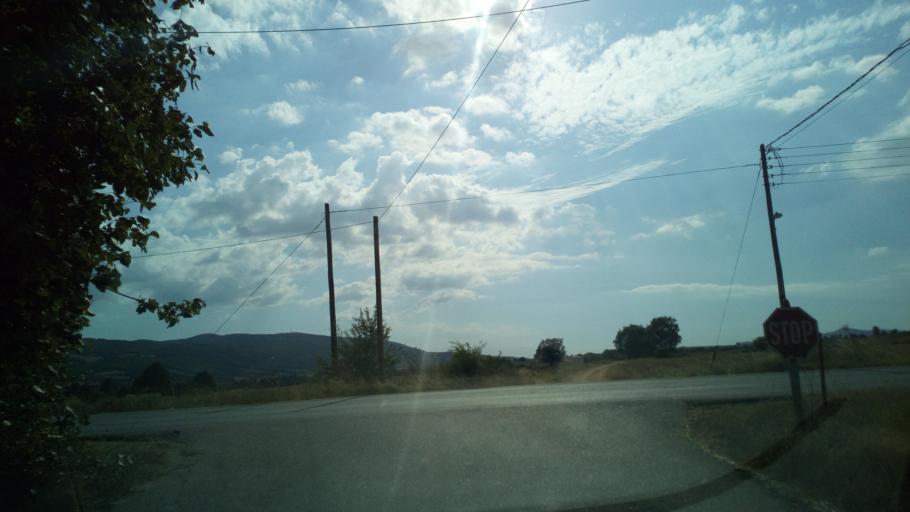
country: GR
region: Central Macedonia
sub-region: Nomos Chalkidikis
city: Polygyros
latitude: 40.4711
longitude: 23.3932
